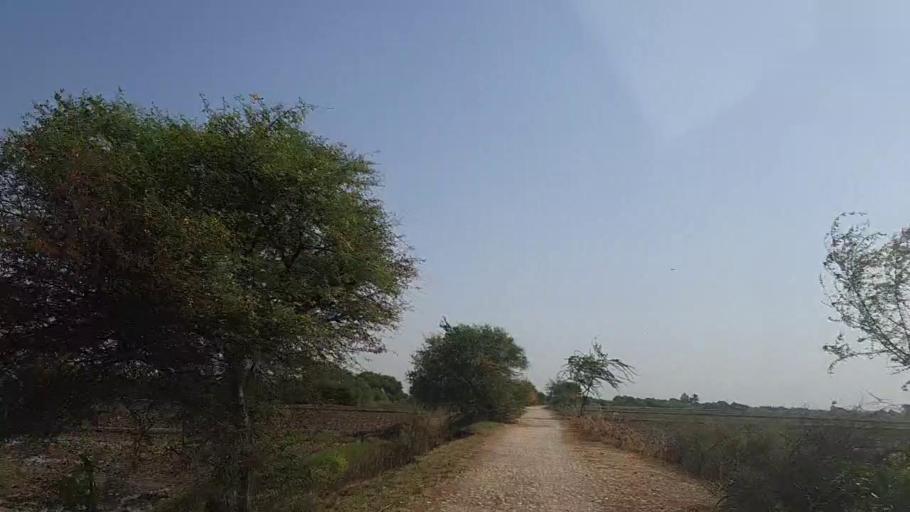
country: PK
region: Sindh
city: Daro Mehar
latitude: 24.7204
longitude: 68.1095
